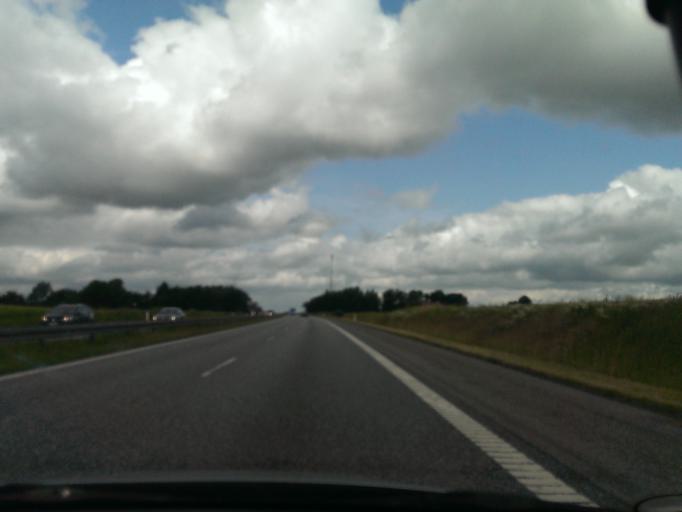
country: DK
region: North Denmark
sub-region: Mariagerfjord Kommune
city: Hobro
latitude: 56.5768
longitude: 9.8353
